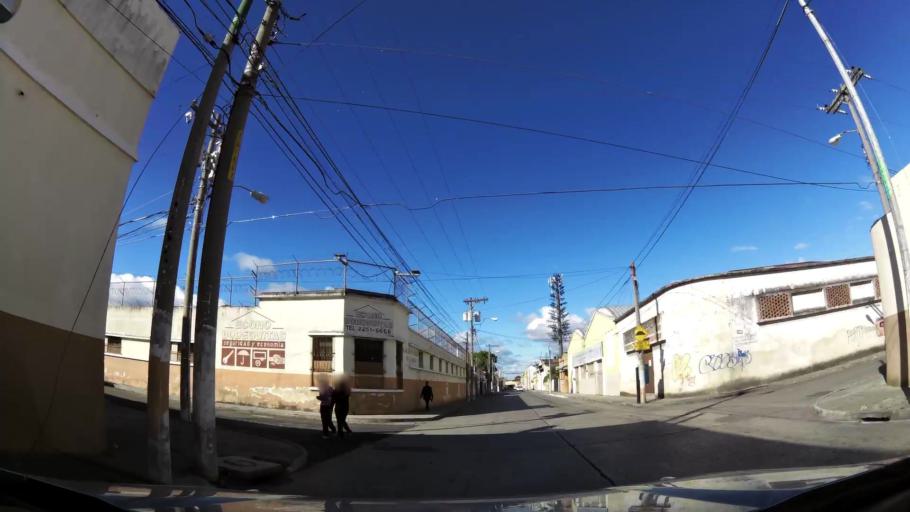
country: GT
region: Guatemala
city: Guatemala City
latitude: 14.6324
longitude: -90.5069
